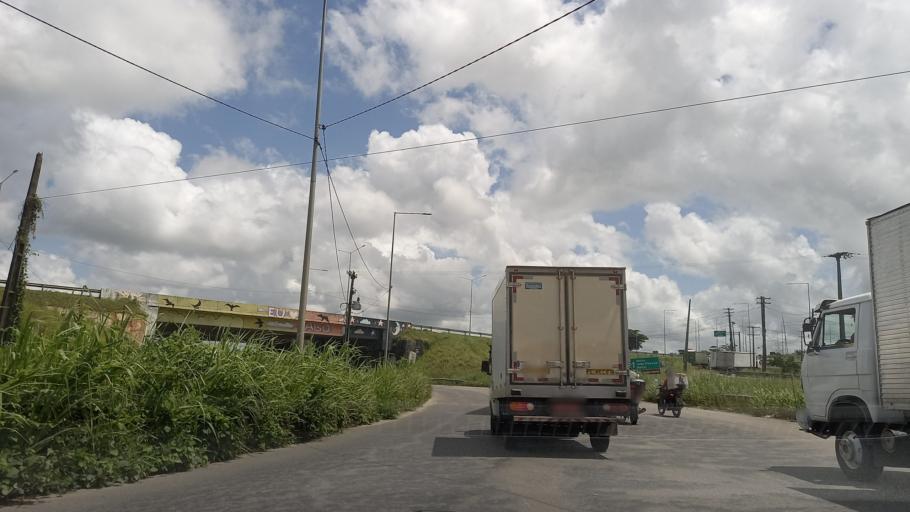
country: BR
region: Pernambuco
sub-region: Cabo De Santo Agostinho
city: Cabo
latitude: -8.2506
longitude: -35.0059
